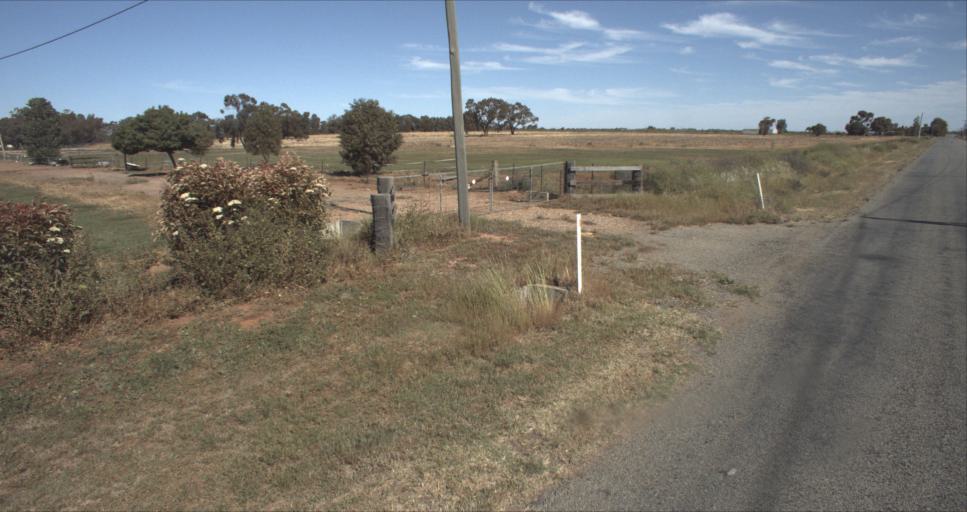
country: AU
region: New South Wales
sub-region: Leeton
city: Leeton
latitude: -34.5599
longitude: 146.3838
